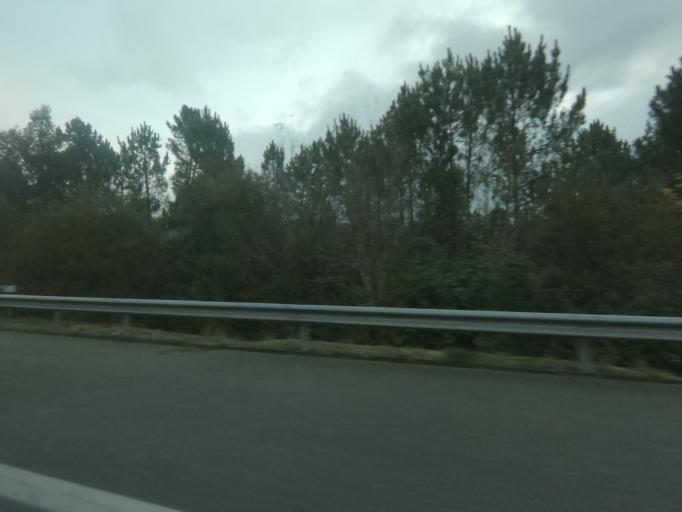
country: PT
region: Braga
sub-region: Barcelos
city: Galegos
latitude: 41.6345
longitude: -8.5615
